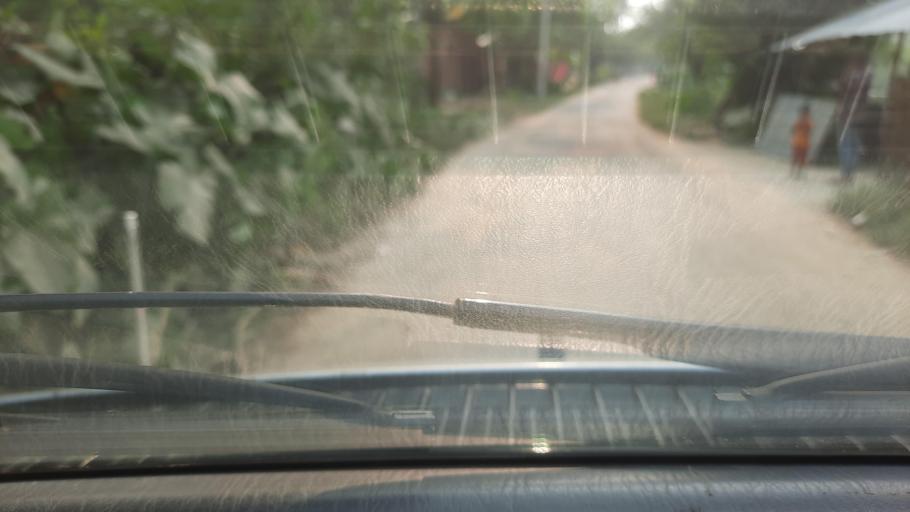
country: BD
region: Khulna
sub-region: Chuadanga
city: Nowlamary
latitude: 23.6031
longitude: 88.8568
